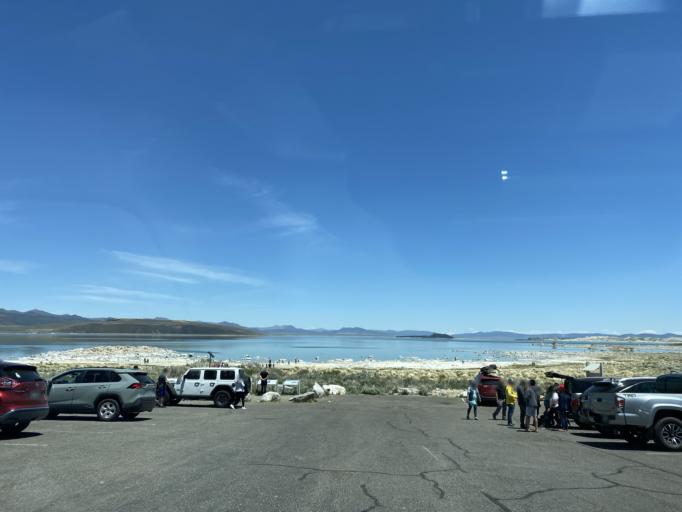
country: US
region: California
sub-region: Mono County
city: Bridgeport
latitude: 37.9768
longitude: -119.1341
